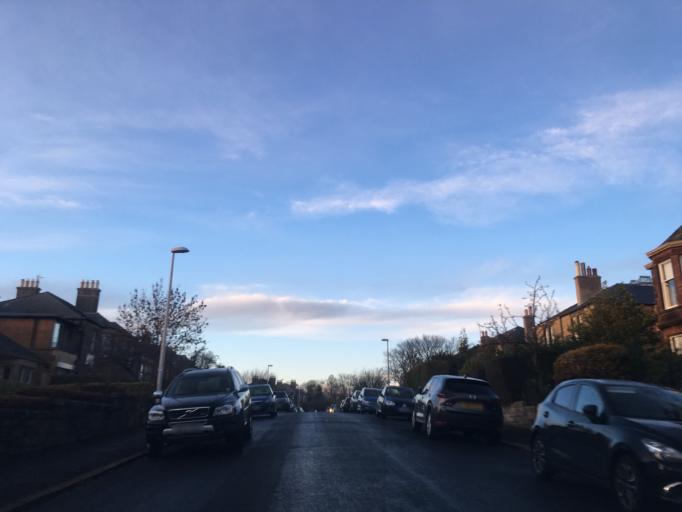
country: GB
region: Scotland
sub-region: Edinburgh
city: Colinton
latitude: 55.9483
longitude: -3.2460
